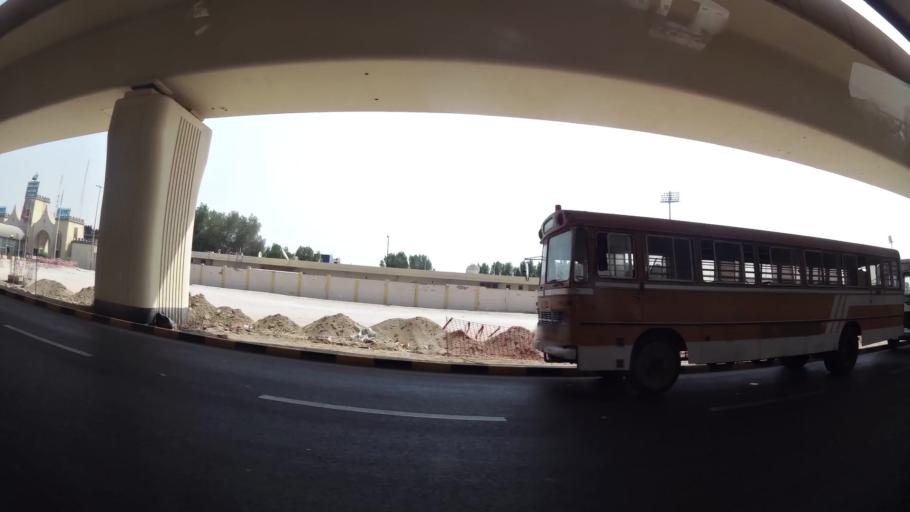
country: KW
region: Al Asimah
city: Ar Rabiyah
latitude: 29.3198
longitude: 47.9049
